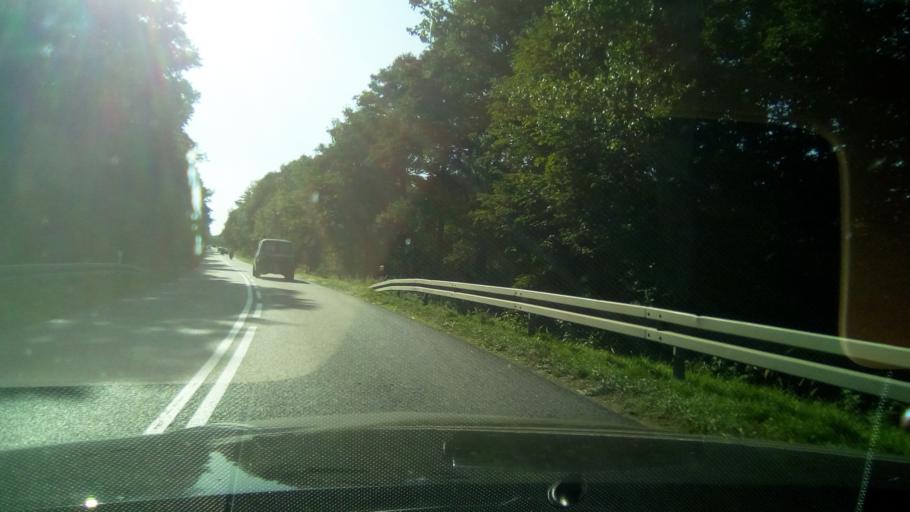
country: PL
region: West Pomeranian Voivodeship
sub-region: Powiat goleniowski
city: Przybiernow
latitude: 53.8257
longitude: 14.8621
